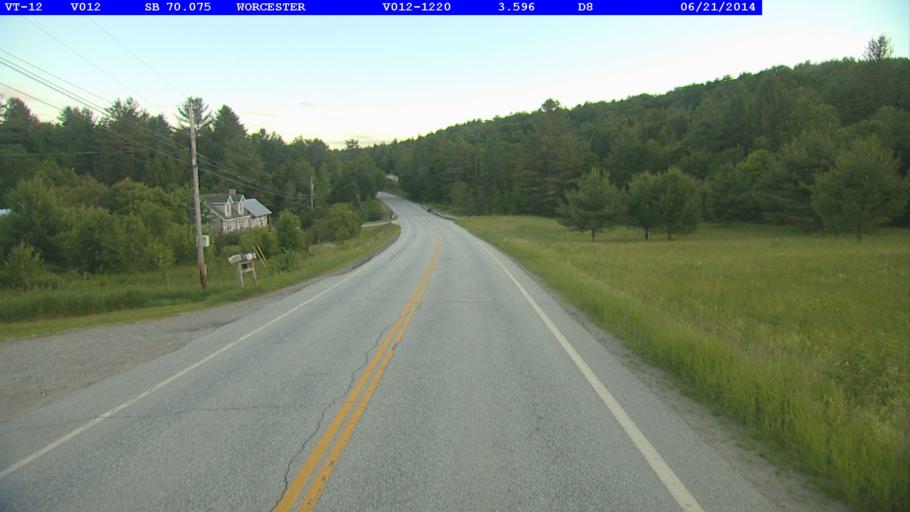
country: US
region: Vermont
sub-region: Washington County
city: Montpelier
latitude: 44.3989
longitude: -72.5546
